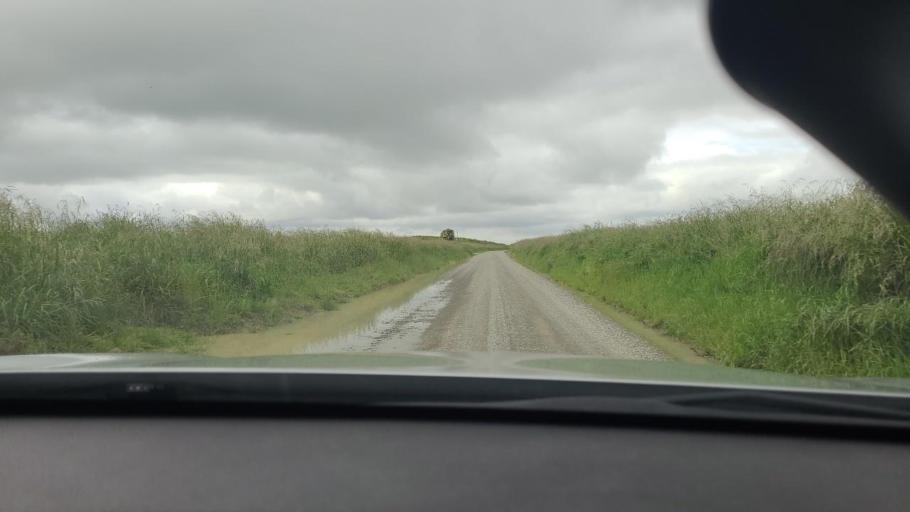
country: NZ
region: Southland
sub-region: Invercargill City
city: Invercargill
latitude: -46.3445
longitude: 168.2437
